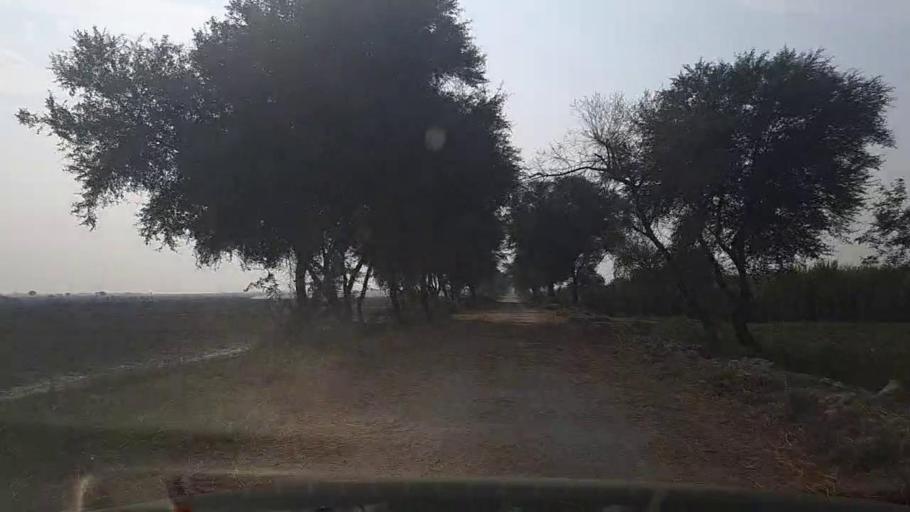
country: PK
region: Sindh
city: Bulri
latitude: 25.0228
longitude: 68.2992
